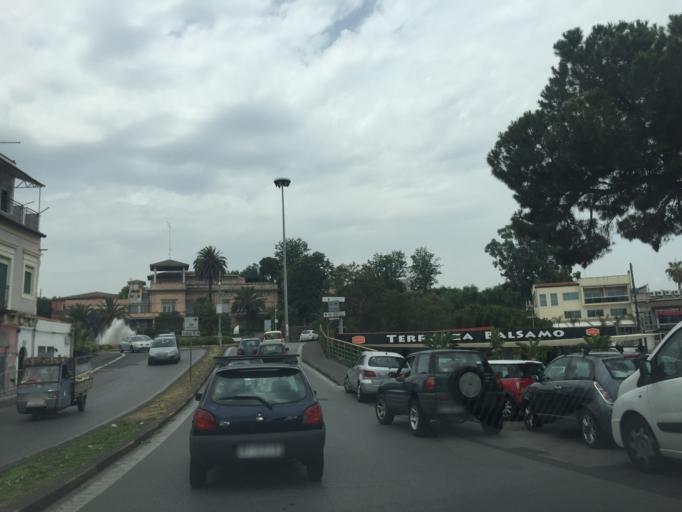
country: IT
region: Sicily
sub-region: Catania
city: Cerza
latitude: 37.5309
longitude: 15.1120
